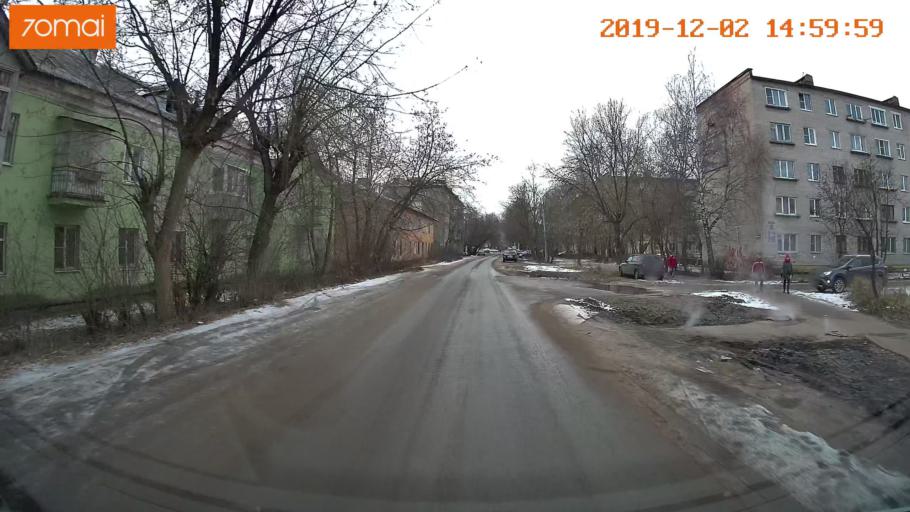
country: RU
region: Ivanovo
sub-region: Gorod Ivanovo
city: Ivanovo
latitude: 56.9707
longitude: 41.0074
